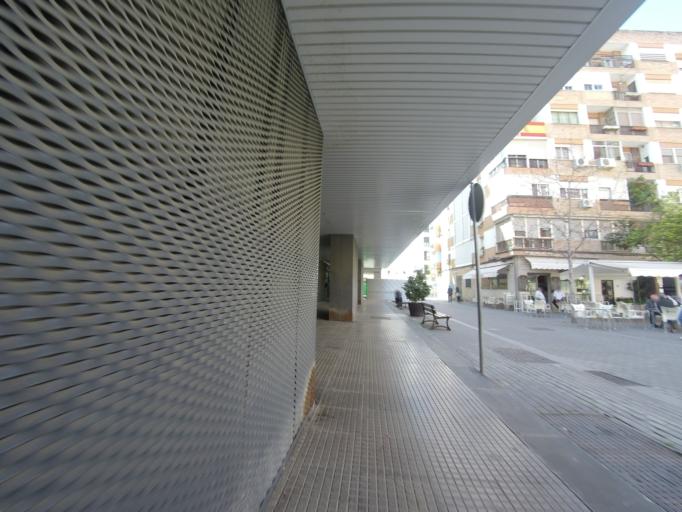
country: ES
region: Andalusia
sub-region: Provincia de Huelva
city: Huelva
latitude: 37.2538
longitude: -6.9531
